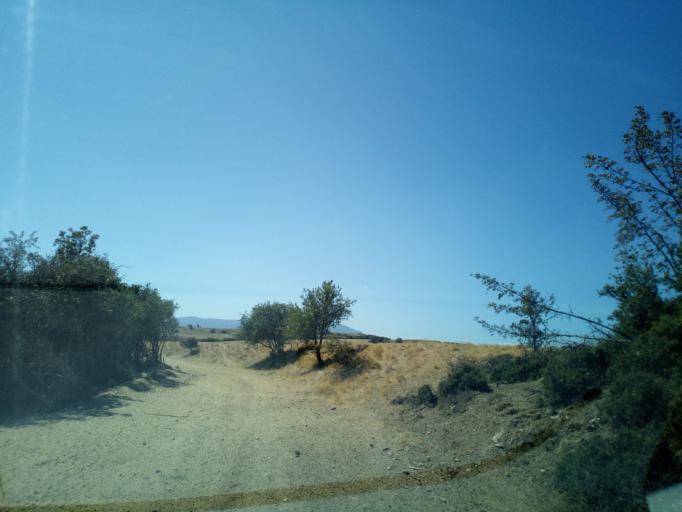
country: GR
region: Central Macedonia
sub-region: Nomos Thessalonikis
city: Kolchikon
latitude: 40.7400
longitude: 23.2505
